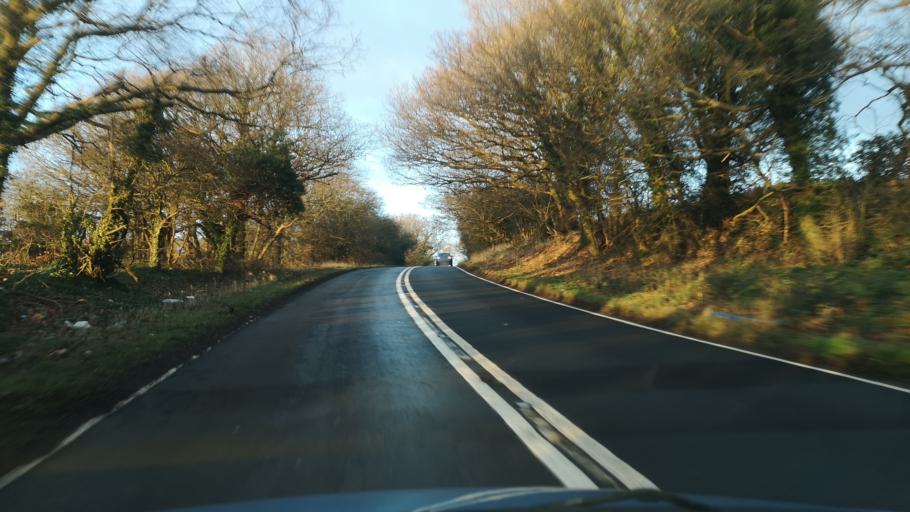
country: GB
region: England
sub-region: Barnsley
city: Great Houghton
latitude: 53.5673
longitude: -1.3502
